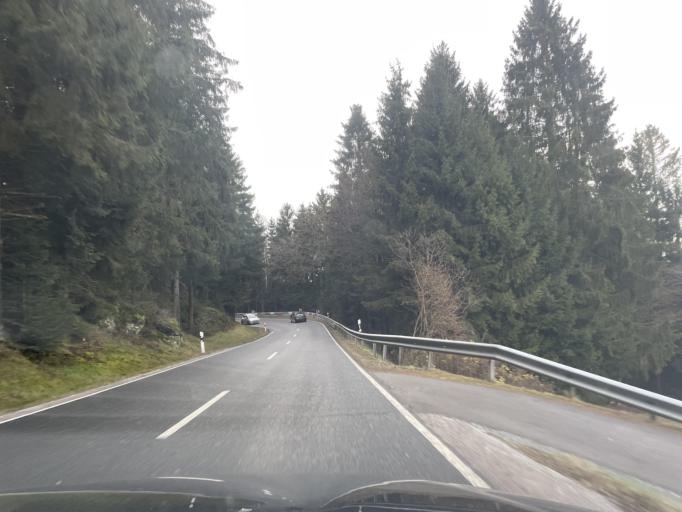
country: DE
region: Bavaria
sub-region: Upper Palatinate
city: Kotzting
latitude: 49.1494
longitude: 12.8839
